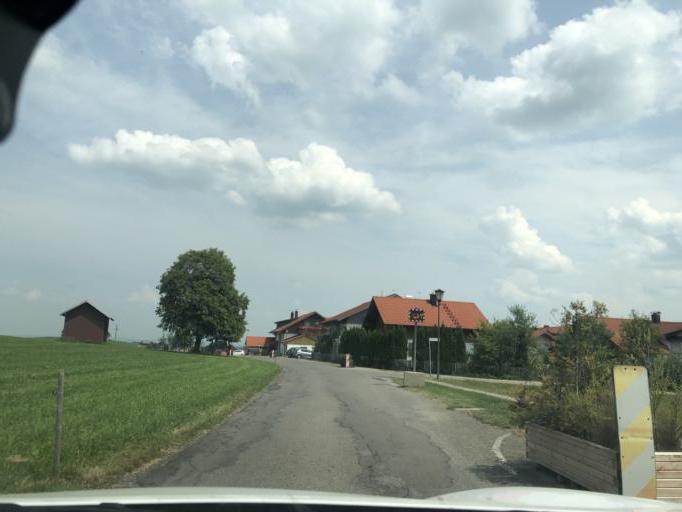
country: DE
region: Bavaria
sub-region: Swabia
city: Oy-Mittelberg
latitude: 47.6411
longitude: 10.4378
